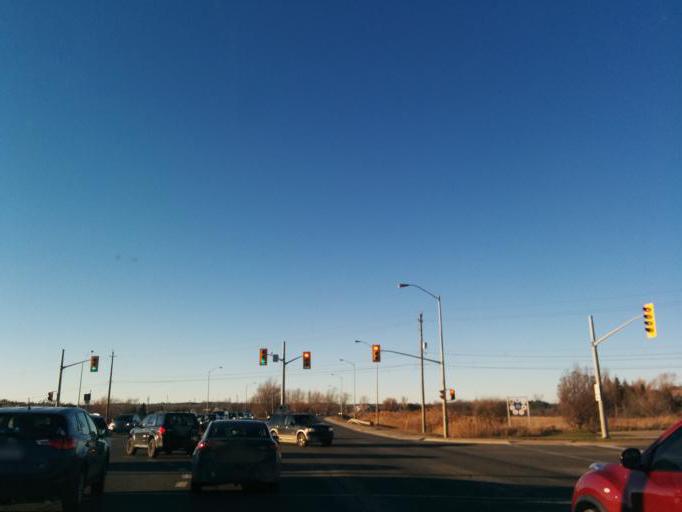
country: CA
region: Ontario
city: Orangeville
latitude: 43.9218
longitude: -80.0826
